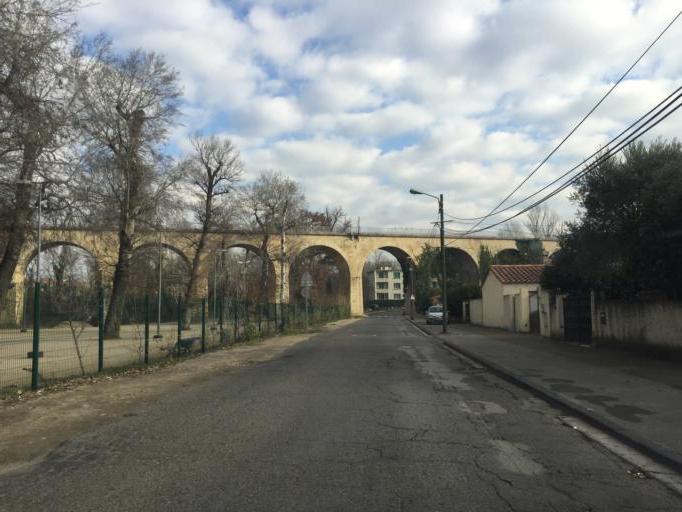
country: FR
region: Provence-Alpes-Cote d'Azur
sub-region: Departement du Vaucluse
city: Carpentras
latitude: 44.0572
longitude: 5.0368
